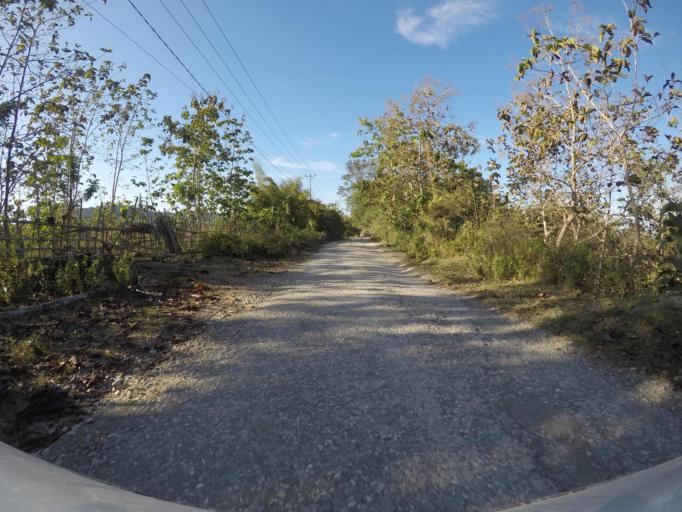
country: TL
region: Viqueque
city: Viqueque
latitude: -8.8739
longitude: 126.3246
